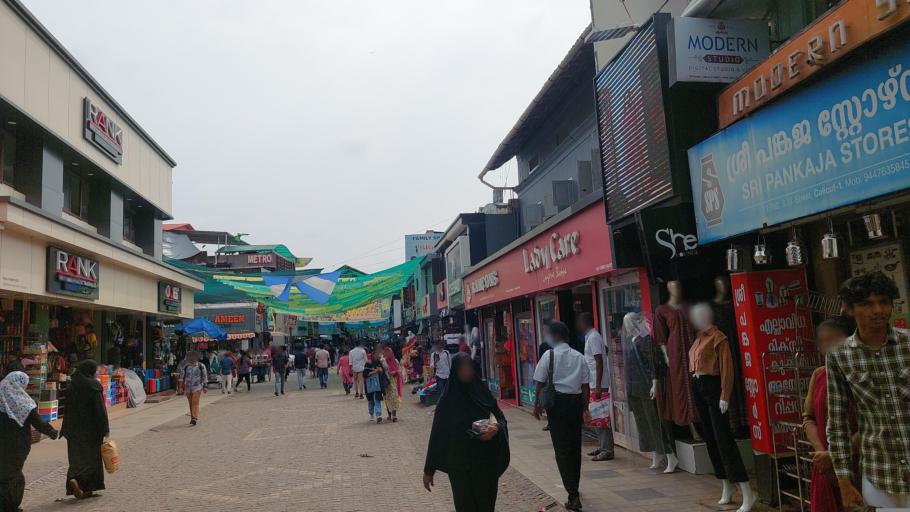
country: IN
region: Kerala
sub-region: Kozhikode
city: Kozhikode
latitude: 11.2501
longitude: 75.7816
